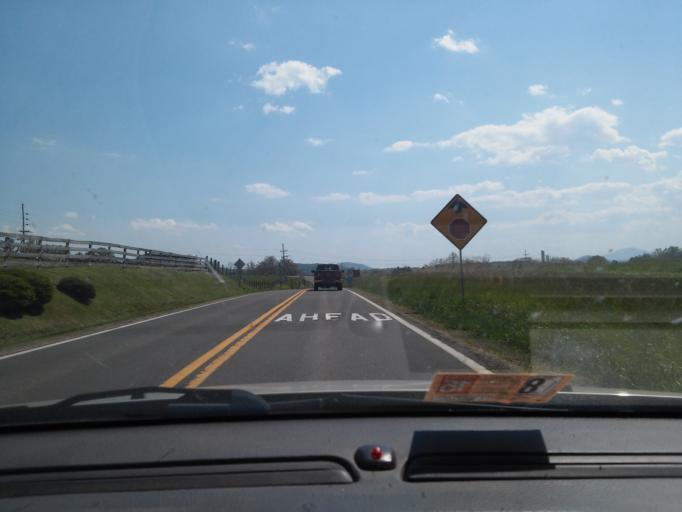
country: US
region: Virginia
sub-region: Rappahannock County
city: Washington
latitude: 38.7275
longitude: -78.1133
